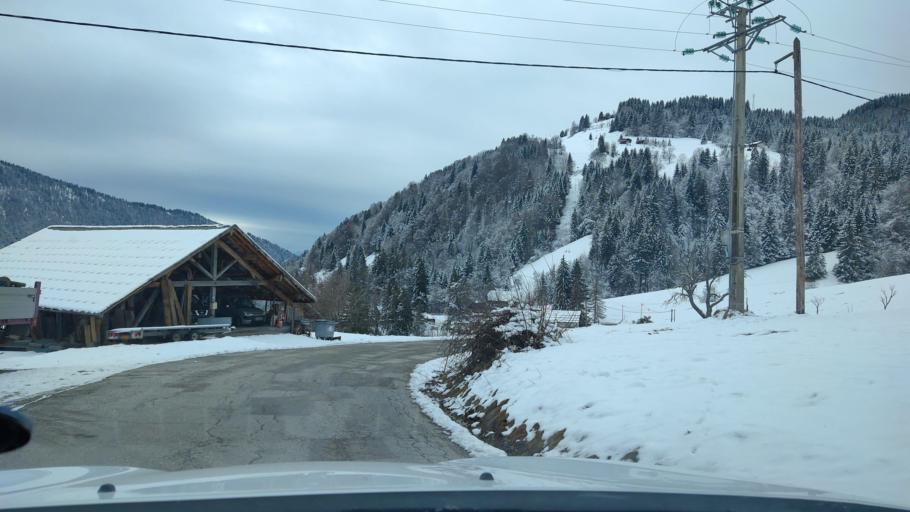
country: FR
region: Rhone-Alpes
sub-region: Departement de la Savoie
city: Ugine
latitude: 45.7766
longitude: 6.4741
